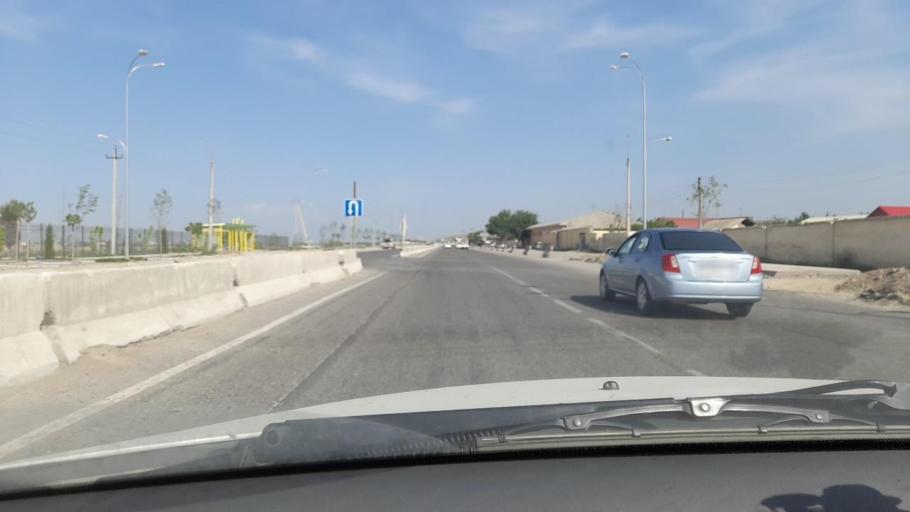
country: UZ
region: Samarqand
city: Samarqand
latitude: 39.7065
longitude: 66.9933
